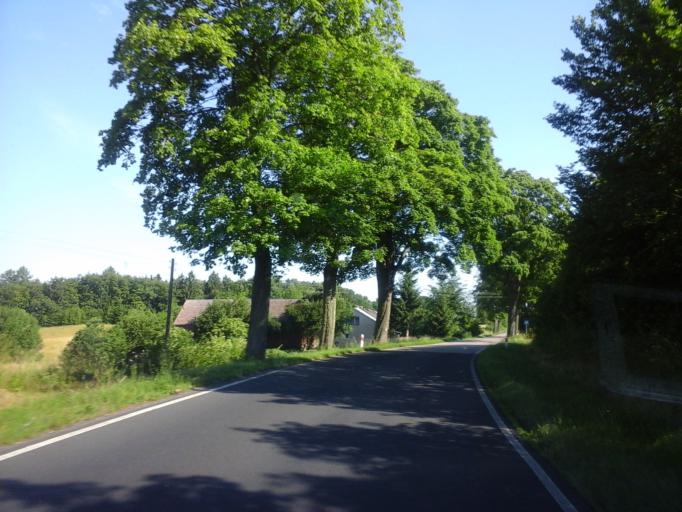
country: PL
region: West Pomeranian Voivodeship
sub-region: Powiat drawski
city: Zlocieniec
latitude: 53.6186
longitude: 15.9224
